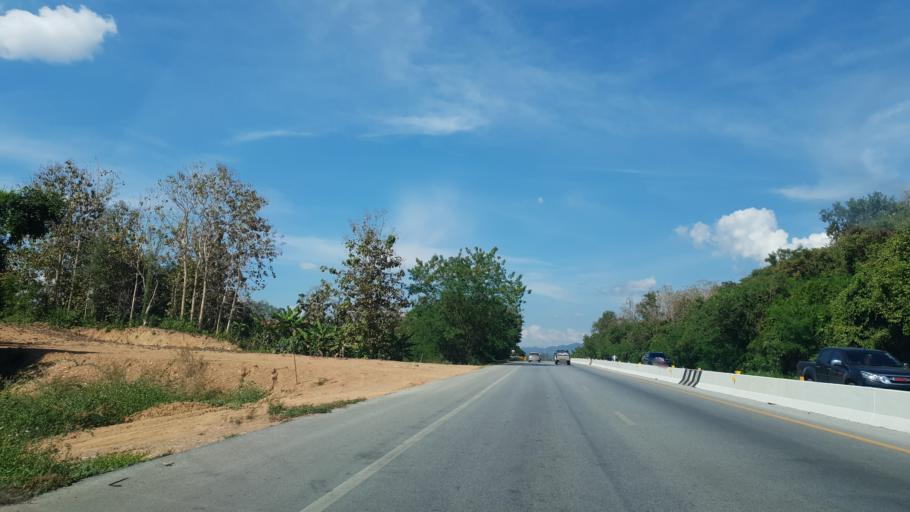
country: TH
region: Uttaradit
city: Uttaradit
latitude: 17.7227
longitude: 100.1347
